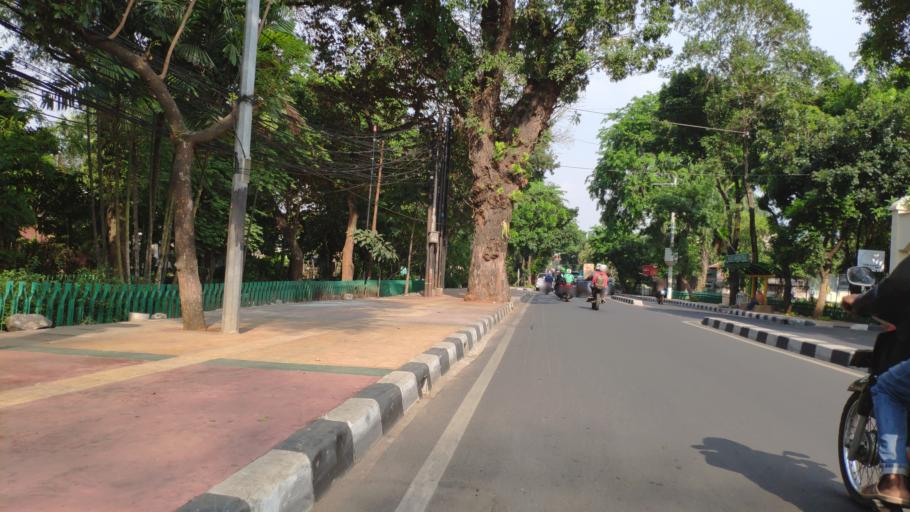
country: ID
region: Jakarta Raya
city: Jakarta
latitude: -6.2861
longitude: 106.8311
